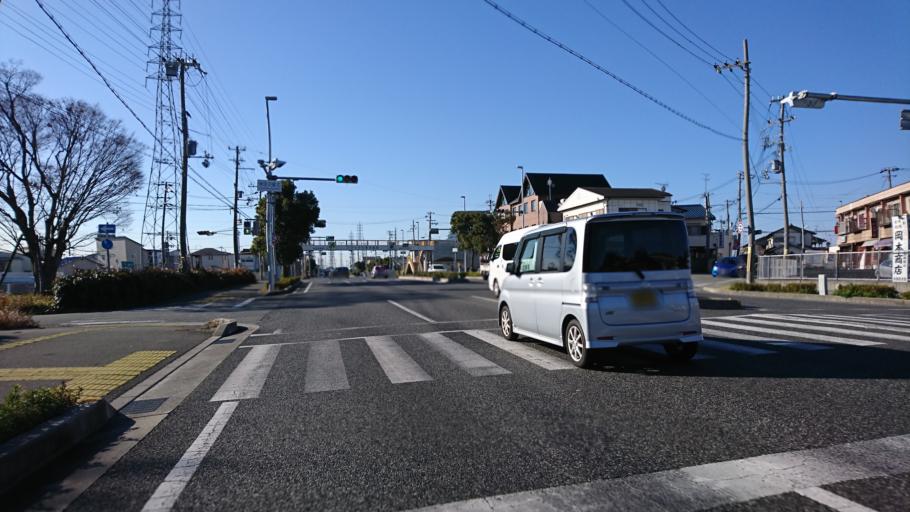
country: JP
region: Hyogo
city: Kakogawacho-honmachi
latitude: 34.7759
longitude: 134.8122
